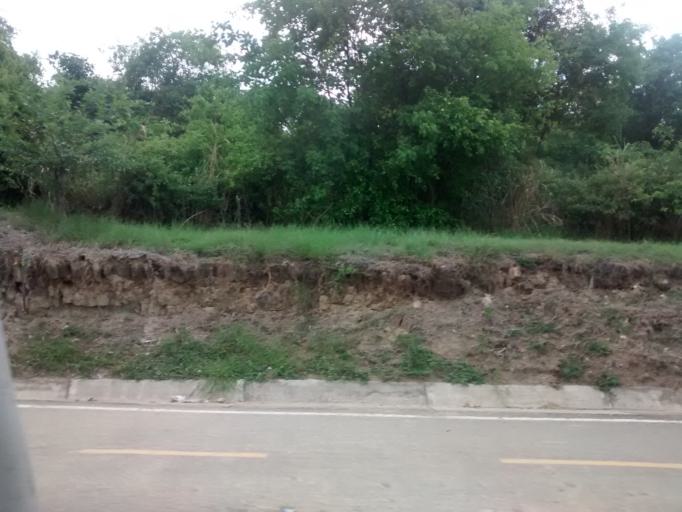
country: CO
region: Cundinamarca
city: Ricaurte
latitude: 4.2746
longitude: -74.7574
